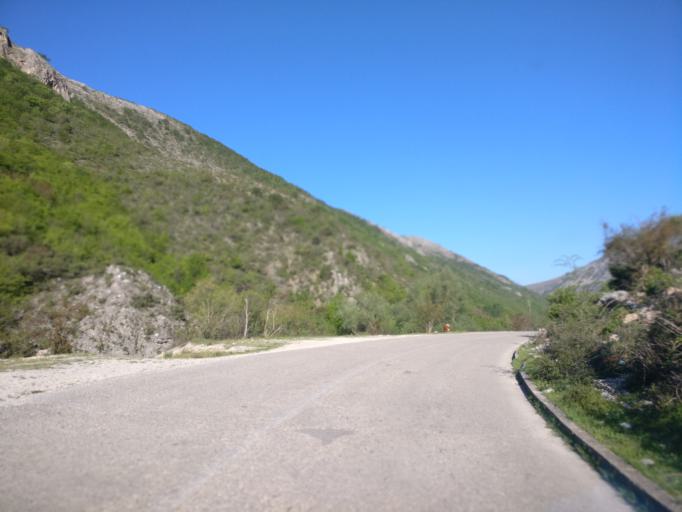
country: BA
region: Federation of Bosnia and Herzegovina
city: Stolac
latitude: 43.0831
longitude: 18.0089
